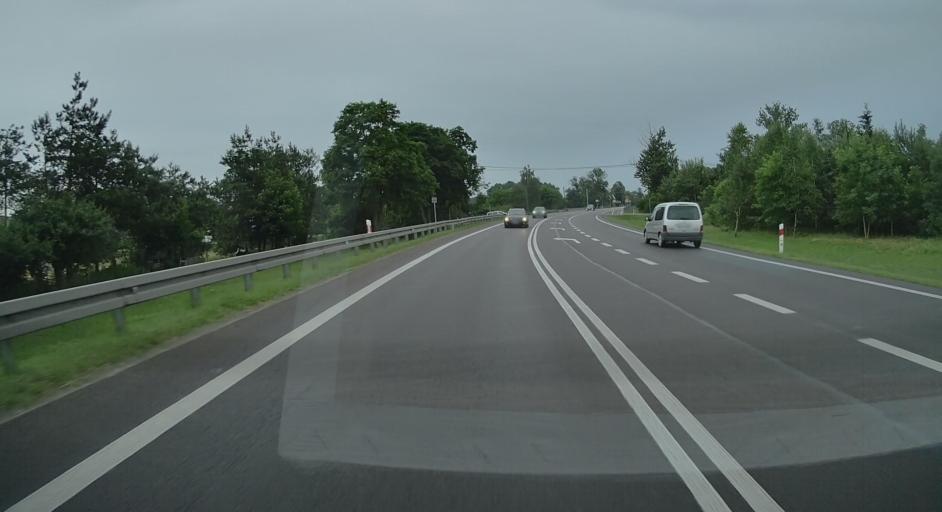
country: PL
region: Lublin Voivodeship
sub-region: Powiat bialski
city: Miedzyrzec Podlaski
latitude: 52.0278
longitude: 22.8670
